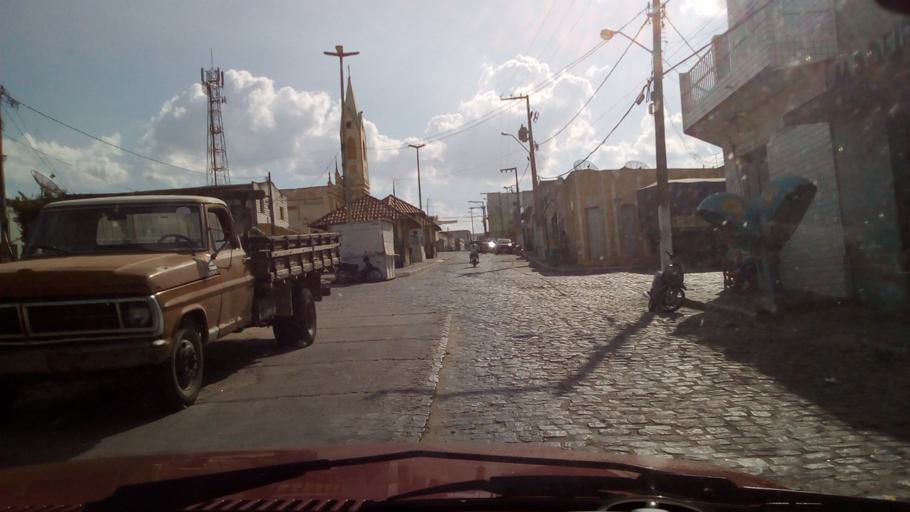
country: BR
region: Paraiba
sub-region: Arara
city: Arara
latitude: -6.8284
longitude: -35.7588
